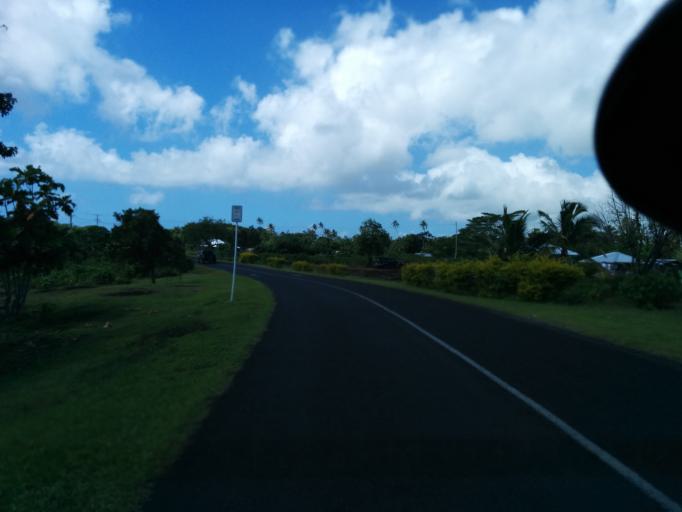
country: WS
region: Gagaifomauga
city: Safotu
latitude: -13.4558
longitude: -172.3258
